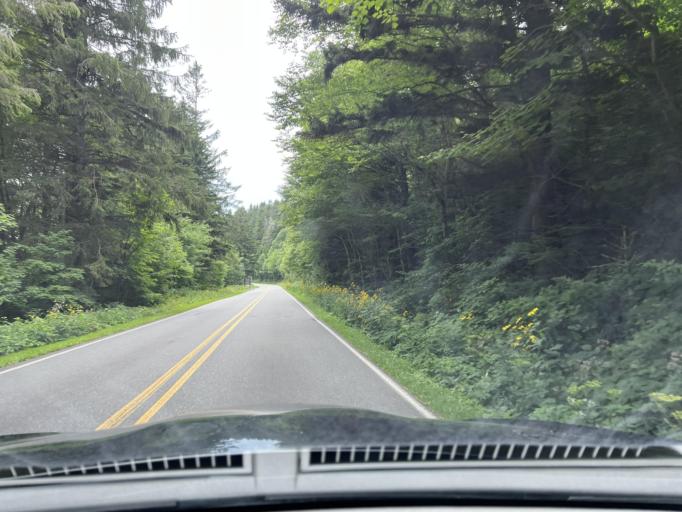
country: US
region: North Carolina
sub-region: Buncombe County
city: Black Mountain
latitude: 35.7290
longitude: -82.2843
